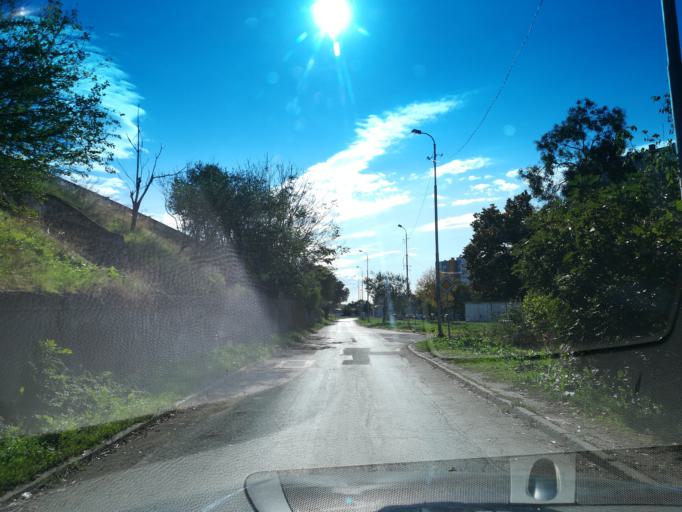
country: BG
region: Stara Zagora
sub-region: Obshtina Stara Zagora
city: Stara Zagora
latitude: 42.4261
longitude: 25.6468
